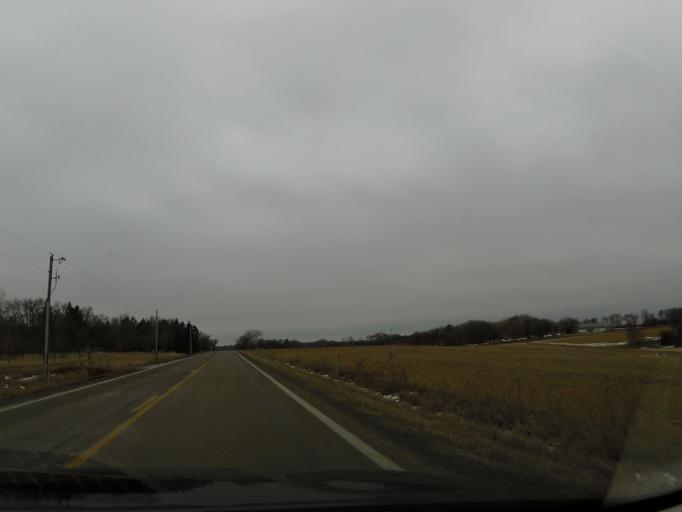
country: US
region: Minnesota
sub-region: Carver County
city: Watertown
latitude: 44.9868
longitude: -93.8490
